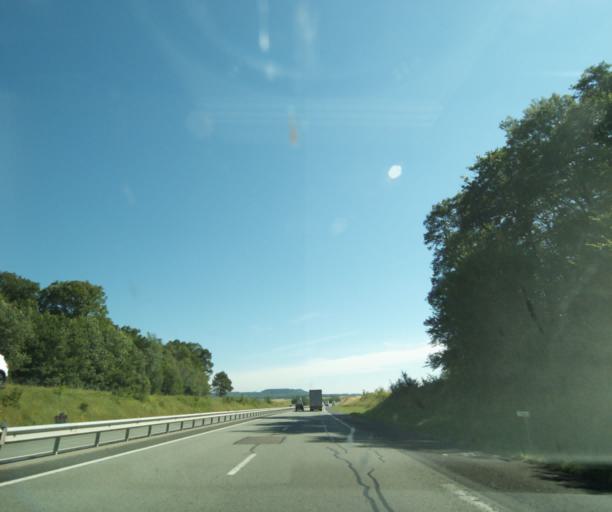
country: FR
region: Lorraine
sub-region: Departement des Vosges
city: Lamarche
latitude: 48.1564
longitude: 5.6964
